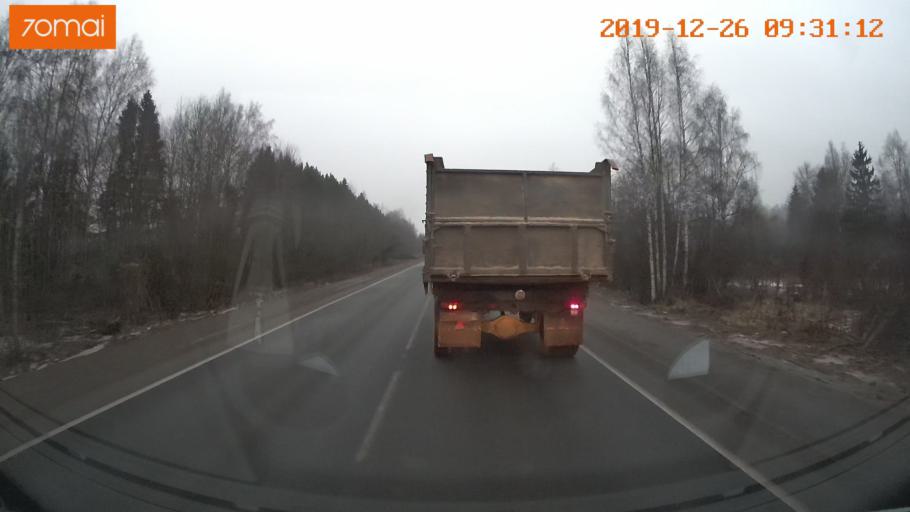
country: RU
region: Vologda
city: Gryazovets
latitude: 59.0672
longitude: 40.1304
